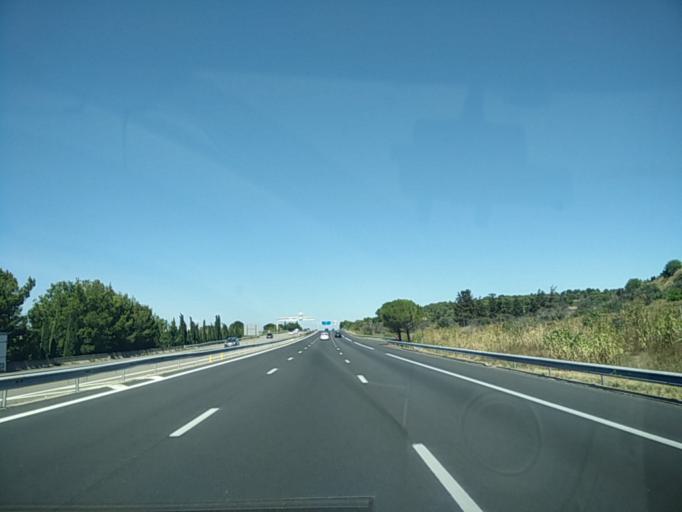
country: FR
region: Provence-Alpes-Cote d'Azur
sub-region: Departement du Vaucluse
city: Vedene
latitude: 43.9709
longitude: 4.8966
